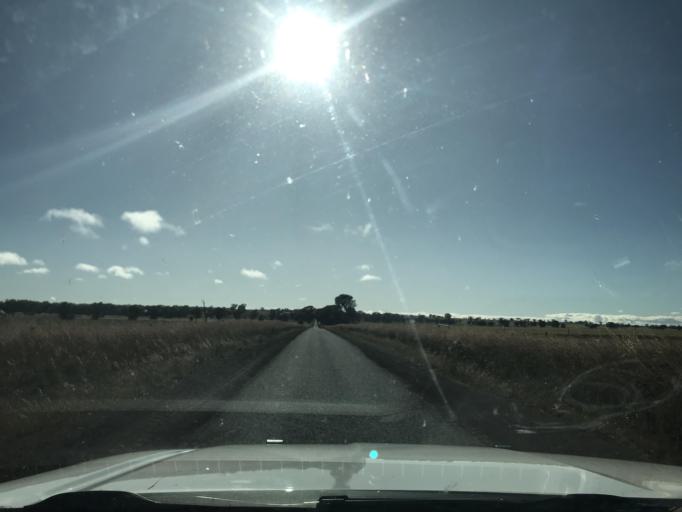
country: AU
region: Victoria
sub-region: Horsham
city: Horsham
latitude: -36.6958
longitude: 141.5820
